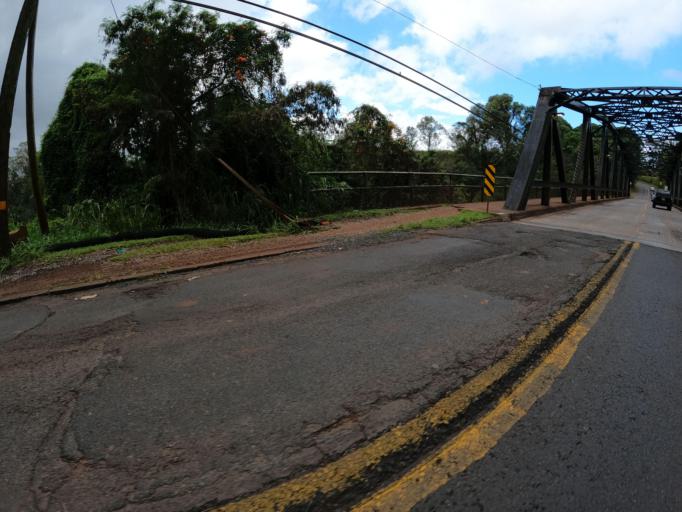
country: US
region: Hawaii
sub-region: Honolulu County
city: Wahiawa
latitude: 21.5006
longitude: -158.0294
